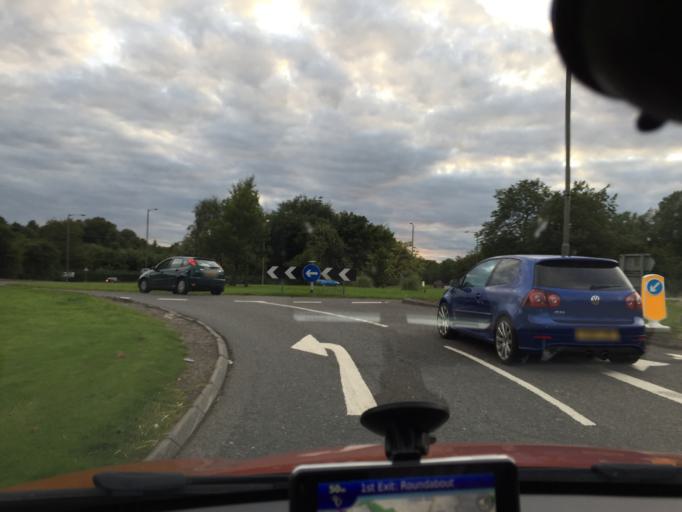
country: GB
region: Scotland
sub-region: Falkirk
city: Bonnybridge
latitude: 56.0127
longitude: -3.8697
